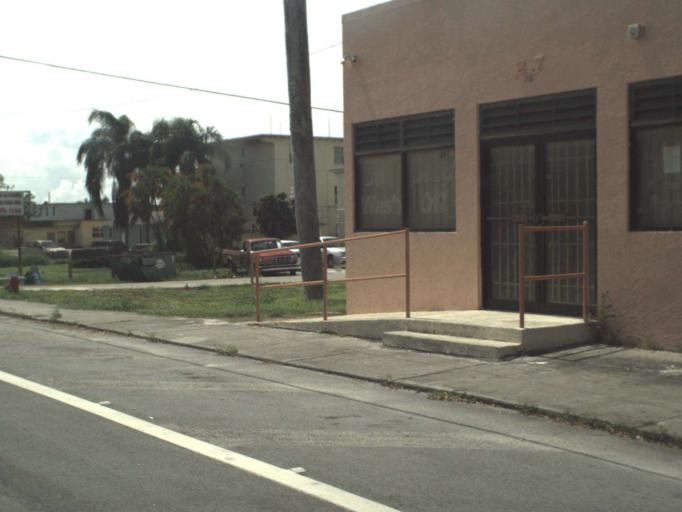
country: US
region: Florida
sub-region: Palm Beach County
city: Pahokee
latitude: 26.8205
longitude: -80.6656
